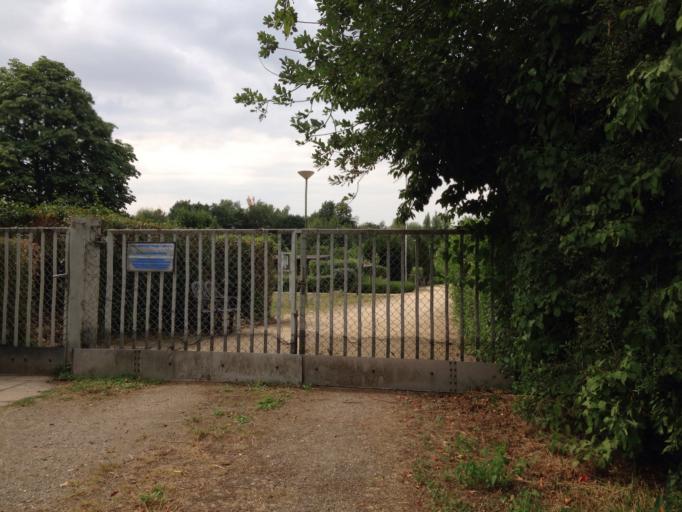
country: DE
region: Hesse
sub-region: Regierungsbezirk Giessen
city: Giessen
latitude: 50.5703
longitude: 8.7004
